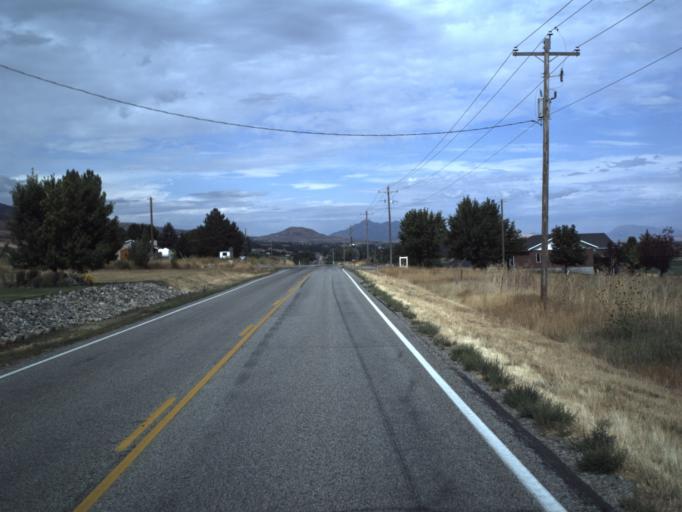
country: US
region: Utah
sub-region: Cache County
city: Wellsville
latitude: 41.6696
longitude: -111.9529
